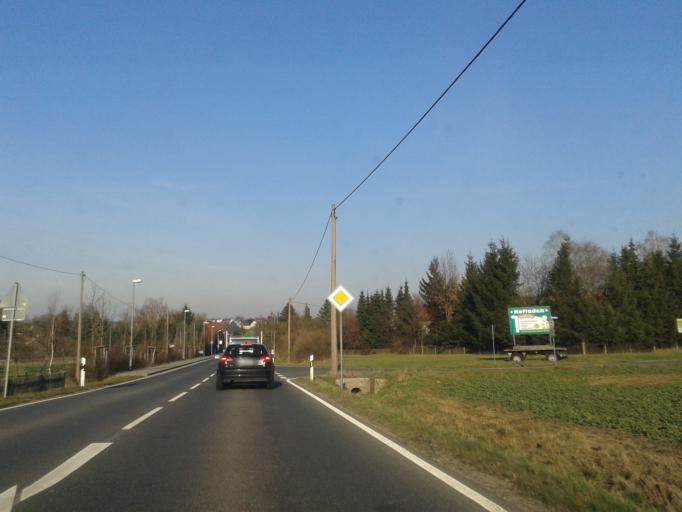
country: DE
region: Saxony
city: Wilsdruff
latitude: 51.0293
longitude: 13.5424
